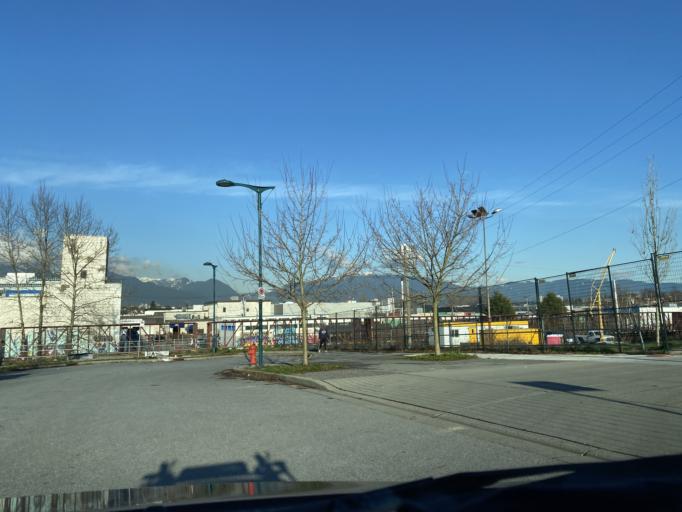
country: CA
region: British Columbia
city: Vancouver
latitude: 49.2681
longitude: -123.0947
